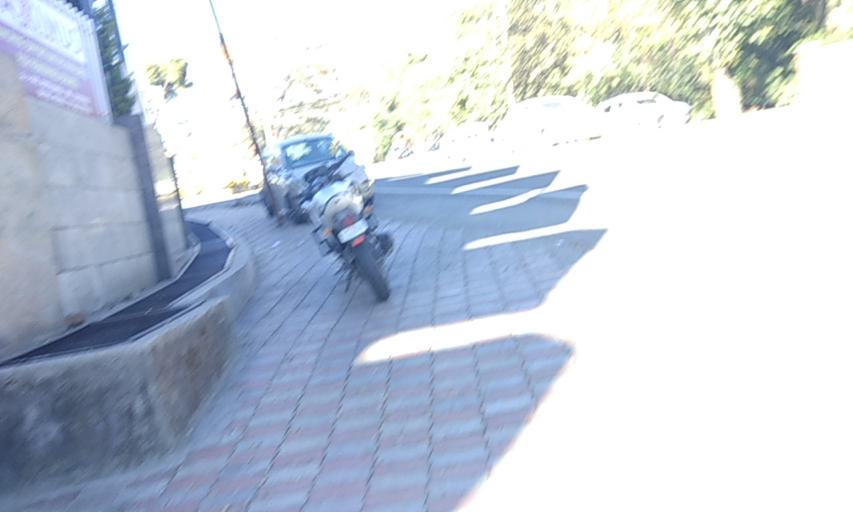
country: IN
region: Himachal Pradesh
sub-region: Kangra
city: Dharmsala
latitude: 32.2142
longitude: 76.3173
